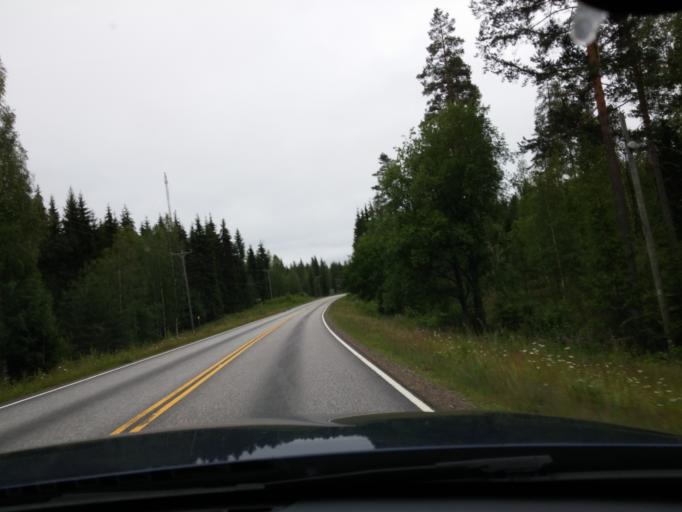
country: FI
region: Central Finland
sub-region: Joutsa
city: Luhanka
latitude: 61.9336
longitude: 25.7266
